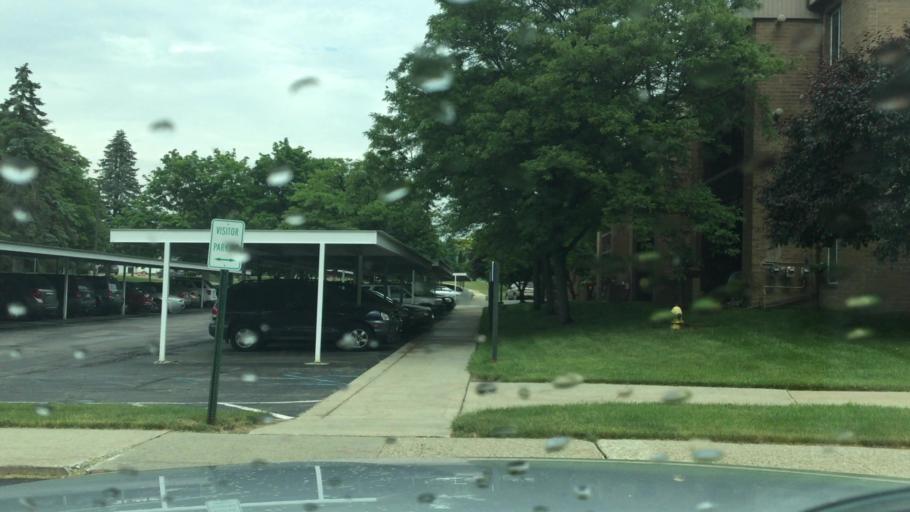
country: US
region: Michigan
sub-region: Lapeer County
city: Lapeer
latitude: 43.0549
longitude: -83.3302
